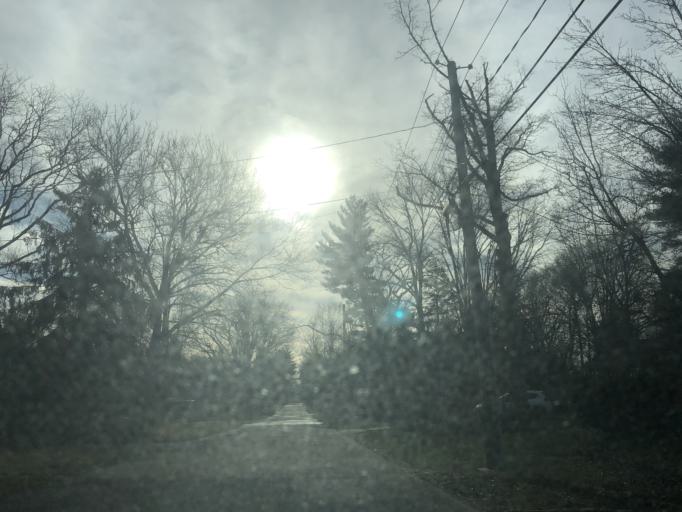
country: US
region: New Jersey
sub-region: Mercer County
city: Princeton
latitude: 40.3503
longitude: -74.6340
